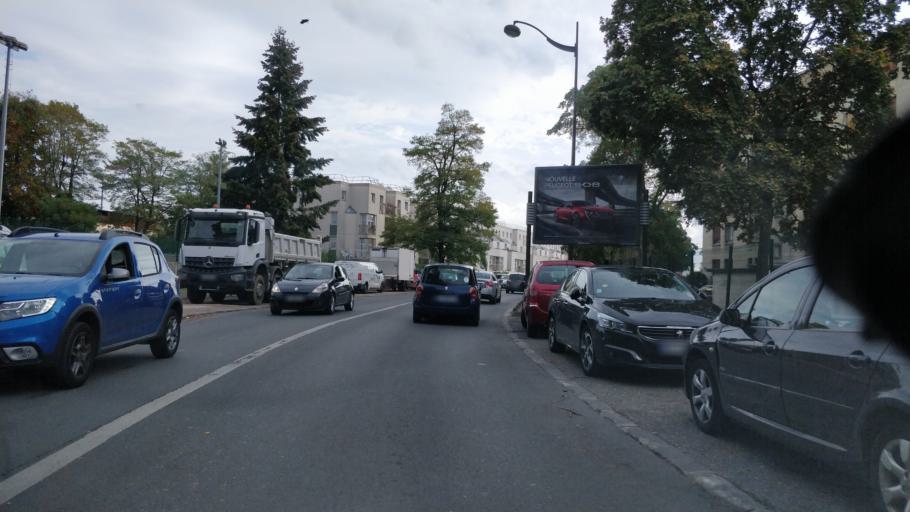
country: FR
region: Ile-de-France
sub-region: Departement de Seine-Saint-Denis
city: Clichy-sous-Bois
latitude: 48.9089
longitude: 2.5502
